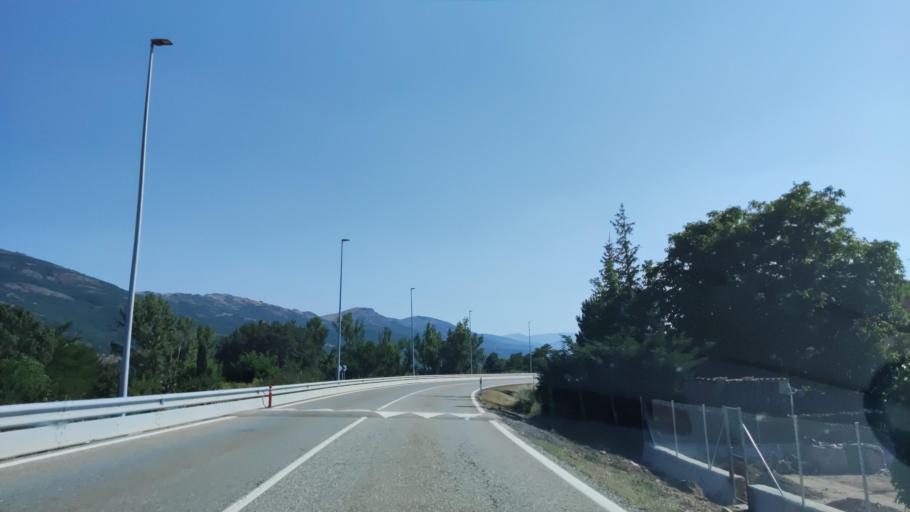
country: ES
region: Madrid
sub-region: Provincia de Madrid
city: Lozoya
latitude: 40.9504
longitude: -3.7877
